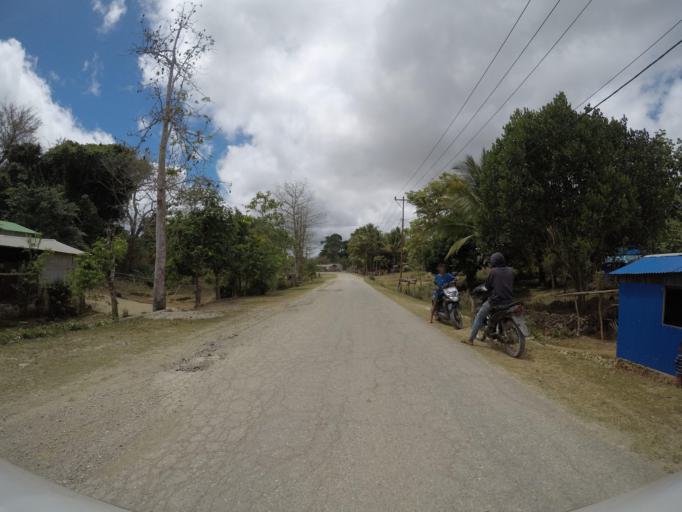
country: TL
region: Lautem
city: Lospalos
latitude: -8.4416
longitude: 126.9641
